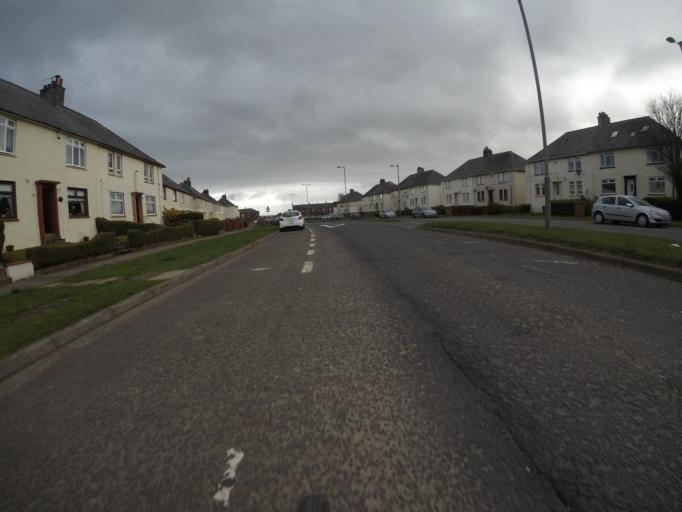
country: GB
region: Scotland
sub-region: East Ayrshire
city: Kilmarnock
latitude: 55.6145
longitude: -4.5144
